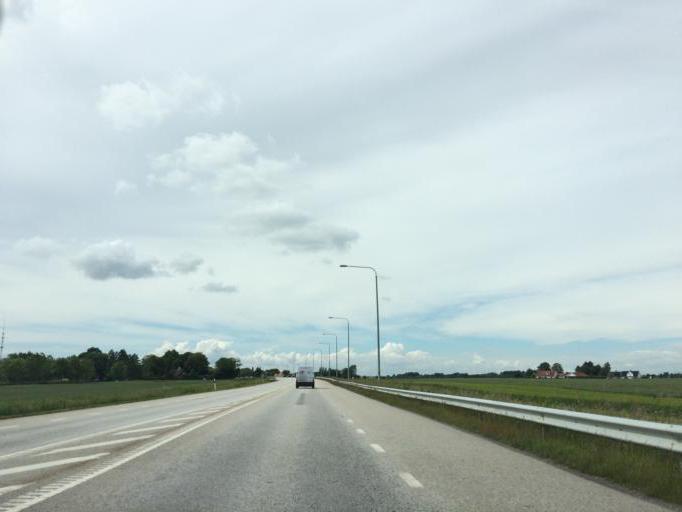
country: SE
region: Skane
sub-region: Staffanstorps Kommun
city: Hjaerup
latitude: 55.7235
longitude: 13.1337
